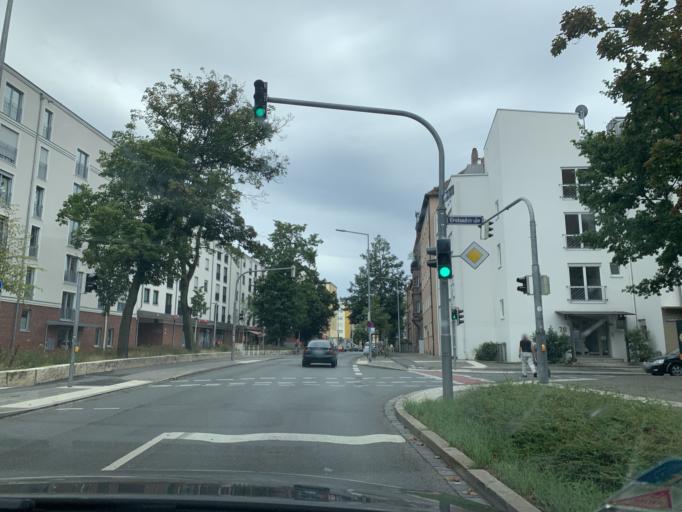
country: DE
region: Bavaria
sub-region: Regierungsbezirk Mittelfranken
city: Nuernberg
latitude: 49.4656
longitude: 11.0819
